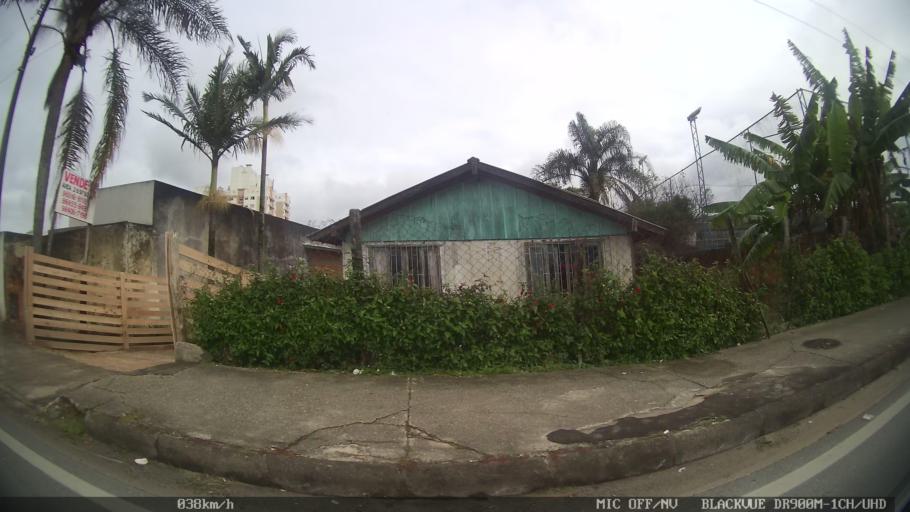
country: BR
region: Santa Catarina
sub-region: Biguacu
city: Biguacu
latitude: -27.5085
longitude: -48.6463
